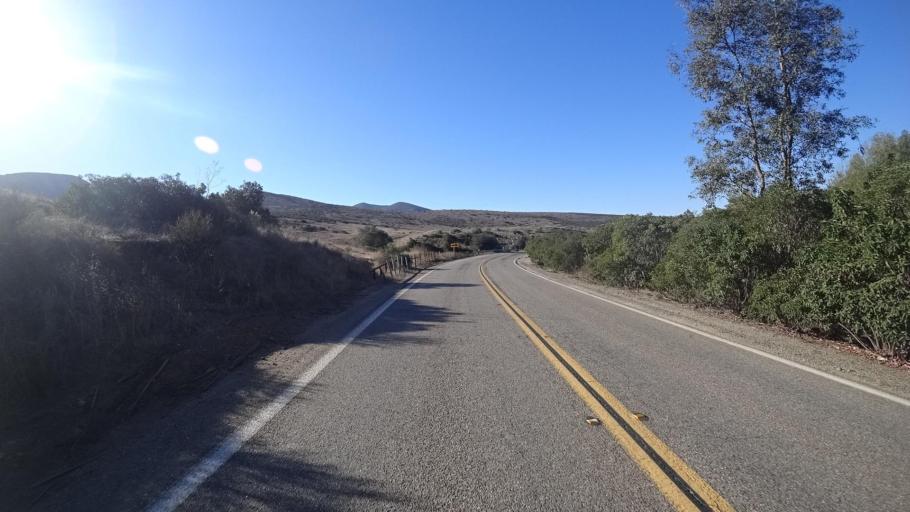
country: US
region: California
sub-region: San Diego County
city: Jamul
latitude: 32.6442
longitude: -116.8700
